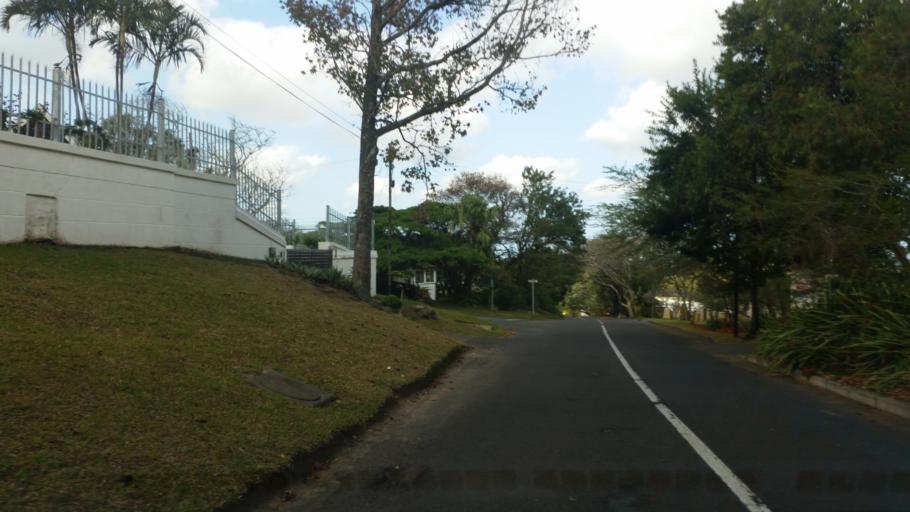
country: ZA
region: KwaZulu-Natal
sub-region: eThekwini Metropolitan Municipality
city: Berea
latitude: -29.8256
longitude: 30.9386
